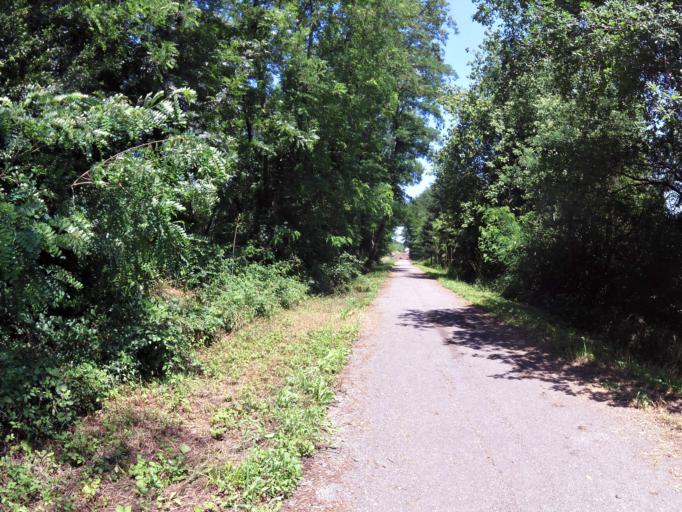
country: FR
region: Aquitaine
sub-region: Departement des Pyrenees-Atlantiques
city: Salies-de-Bearn
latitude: 43.4694
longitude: -0.9372
